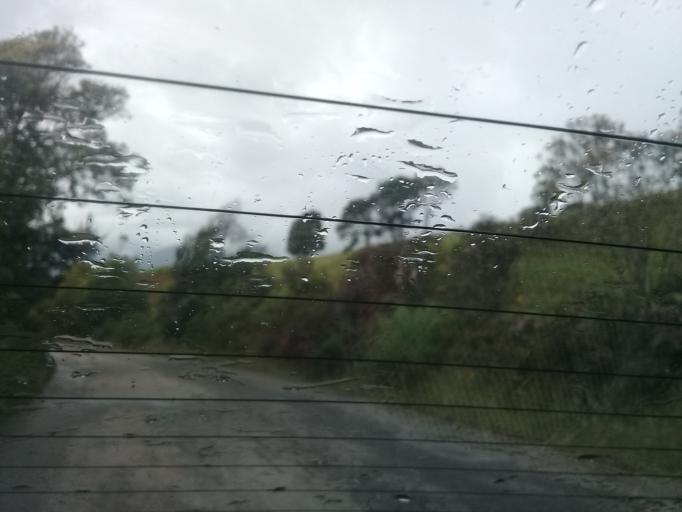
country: CO
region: Cundinamarca
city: Junin
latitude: 4.8379
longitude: -73.7576
